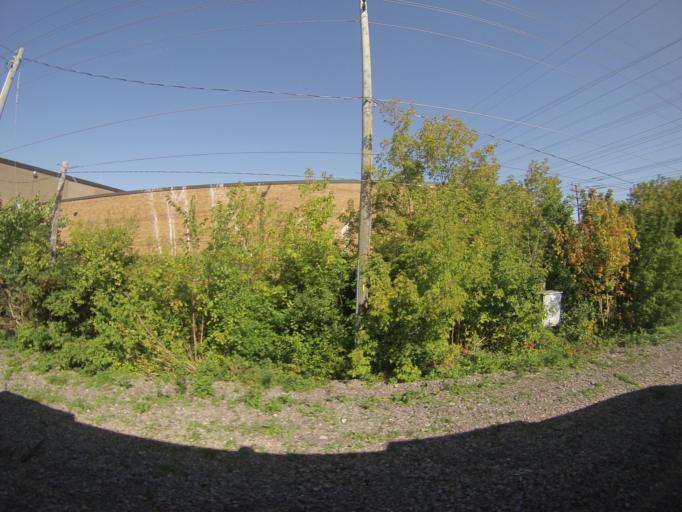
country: CA
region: Ontario
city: Ottawa
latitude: 45.3657
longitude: -75.6626
